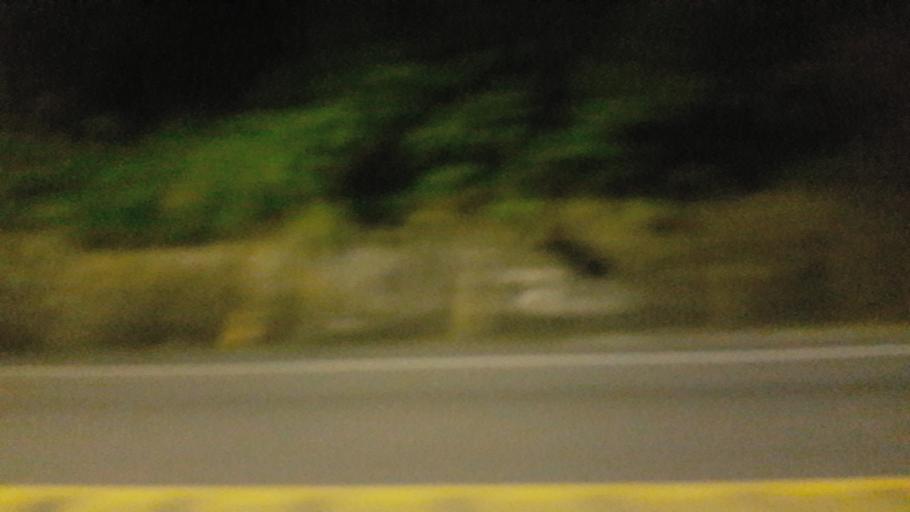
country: TW
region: Taiwan
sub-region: Hsinchu
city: Hsinchu
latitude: 24.7620
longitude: 120.9616
